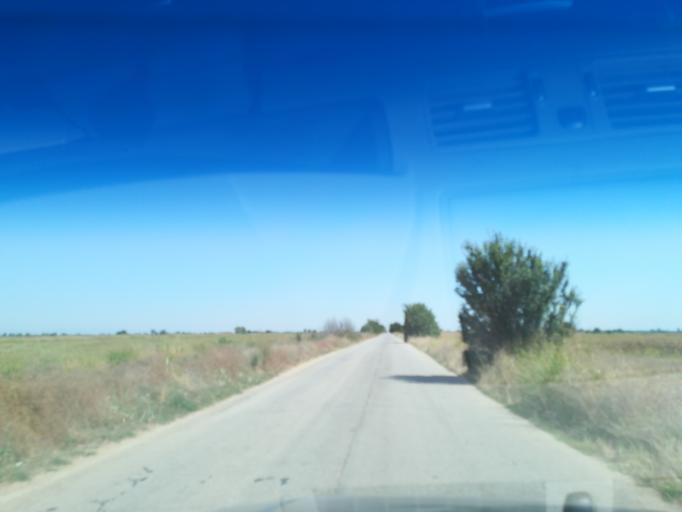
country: BG
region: Plovdiv
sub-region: Obshtina Suedinenie
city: Suedinenie
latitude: 42.2515
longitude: 24.4636
